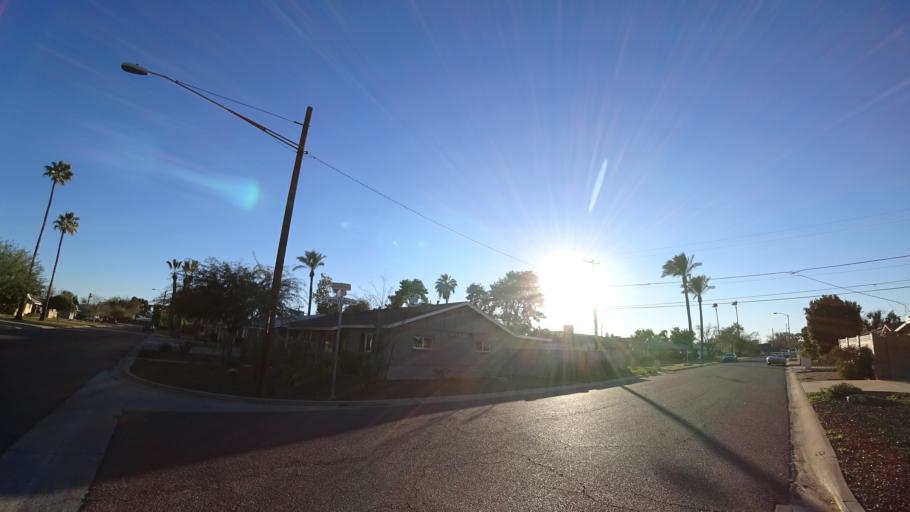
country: US
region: Arizona
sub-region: Maricopa County
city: Phoenix
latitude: 33.4854
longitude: -112.0365
